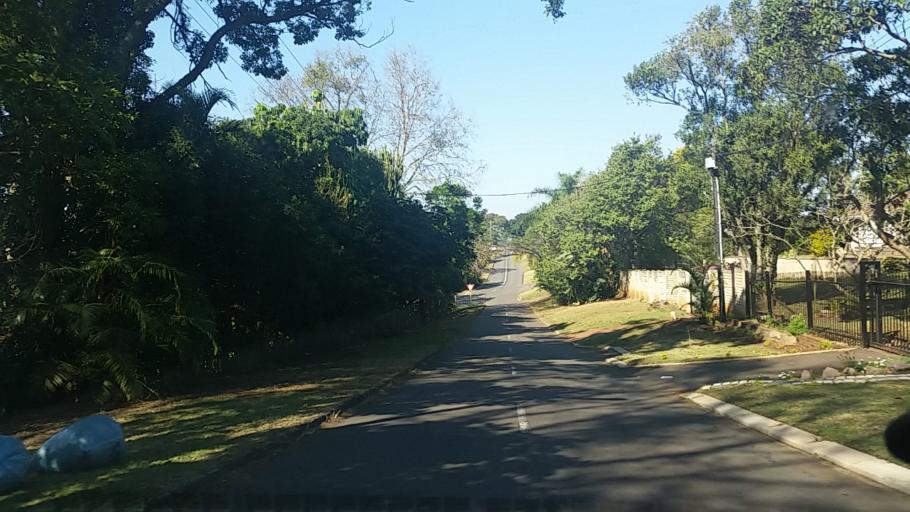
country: ZA
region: KwaZulu-Natal
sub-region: eThekwini Metropolitan Municipality
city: Berea
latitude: -29.8510
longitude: 30.9001
